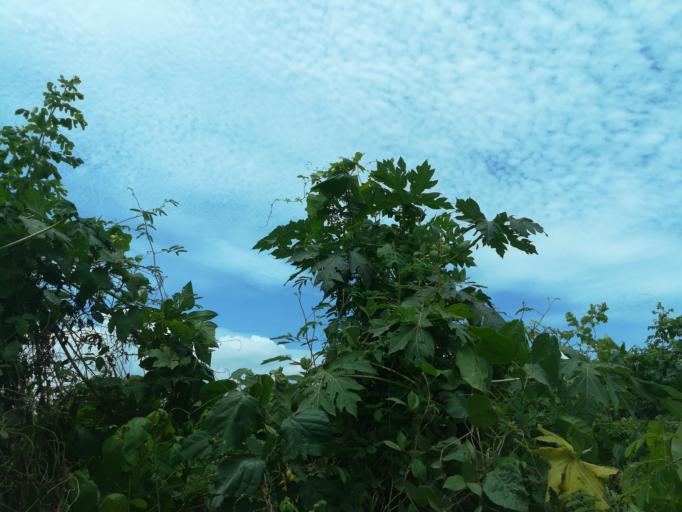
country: NG
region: Lagos
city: Ebute Ikorodu
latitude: 6.5759
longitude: 3.4901
